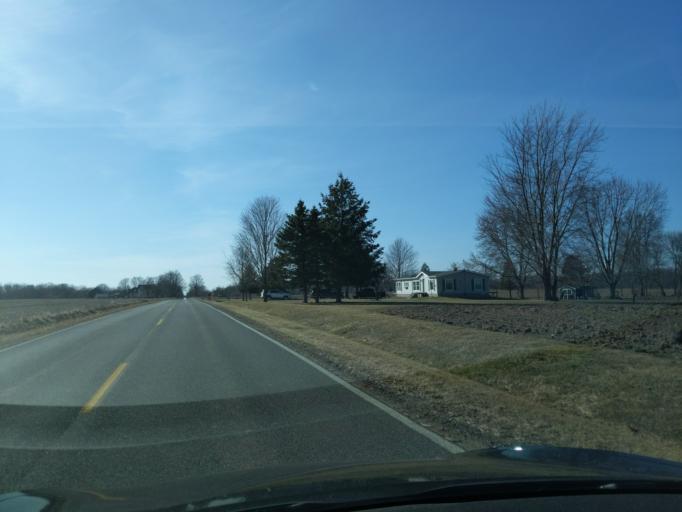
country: US
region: Michigan
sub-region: Ionia County
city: Saranac
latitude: 42.9296
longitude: -85.1475
